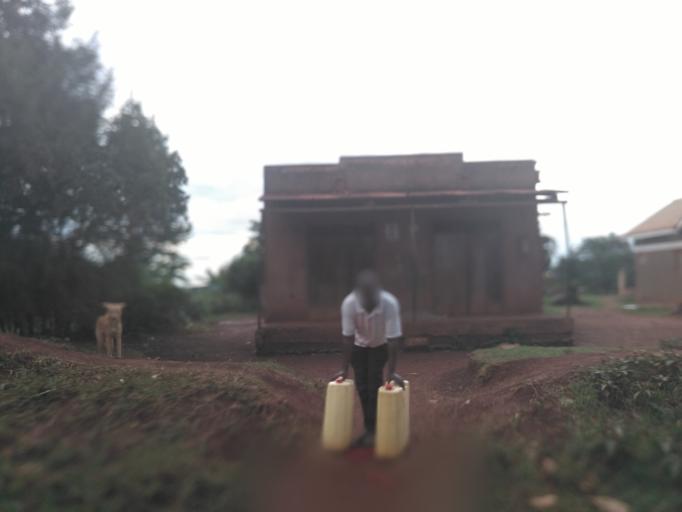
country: UG
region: Central Region
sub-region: Buikwe District
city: Njeru
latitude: 0.4088
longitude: 33.1802
